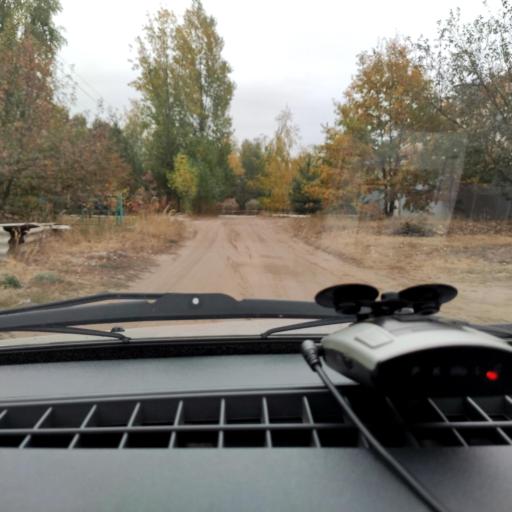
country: RU
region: Voronezj
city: Podgornoye
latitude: 51.7621
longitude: 39.1801
